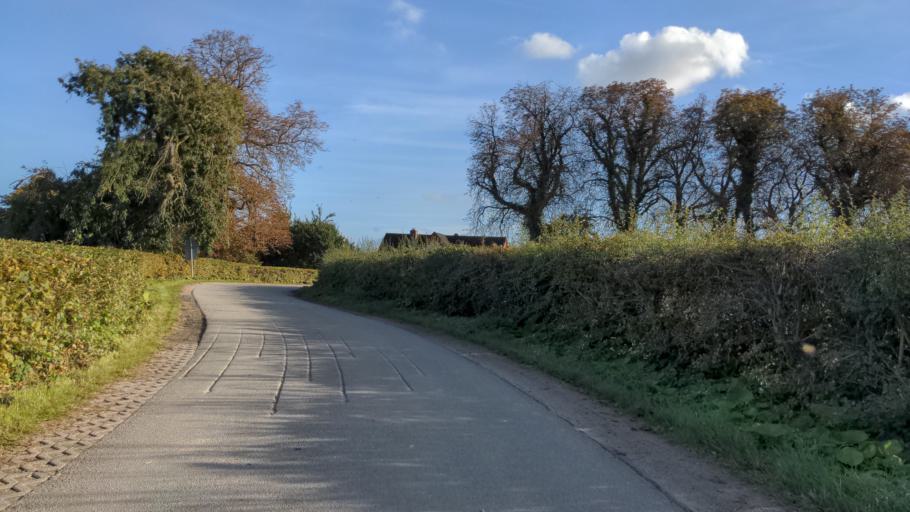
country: DE
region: Schleswig-Holstein
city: Manhagen
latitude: 54.1848
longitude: 10.9096
